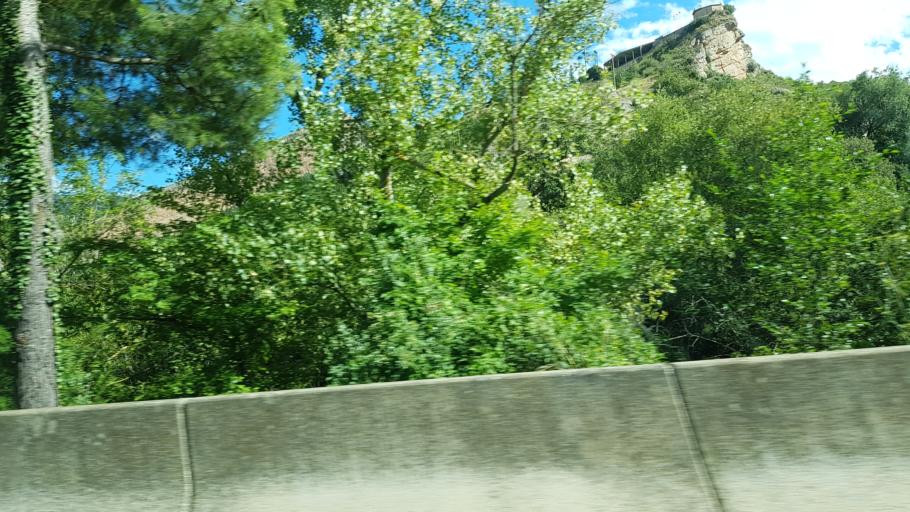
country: ES
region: La Rioja
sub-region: Provincia de La Rioja
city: Viguera
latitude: 42.3137
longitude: -2.5367
